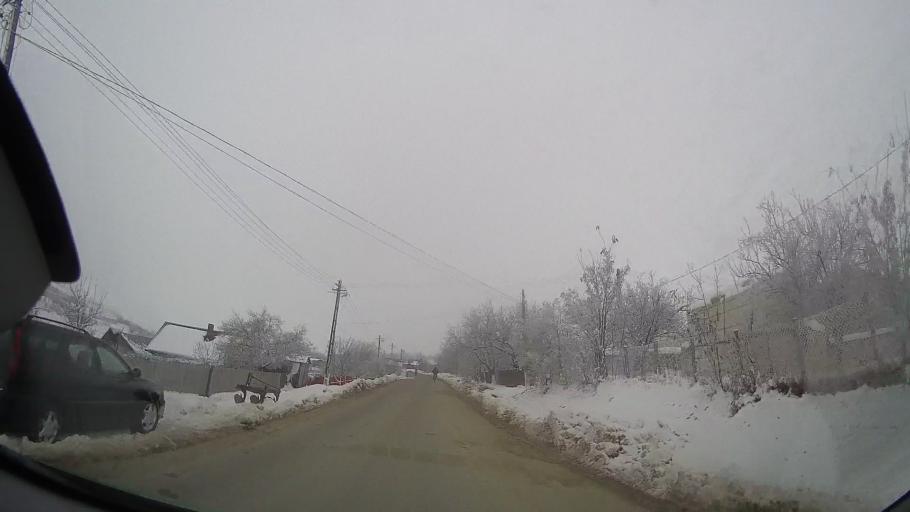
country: RO
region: Neamt
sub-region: Comuna Pancesti
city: Pancesti
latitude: 46.9097
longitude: 27.1585
